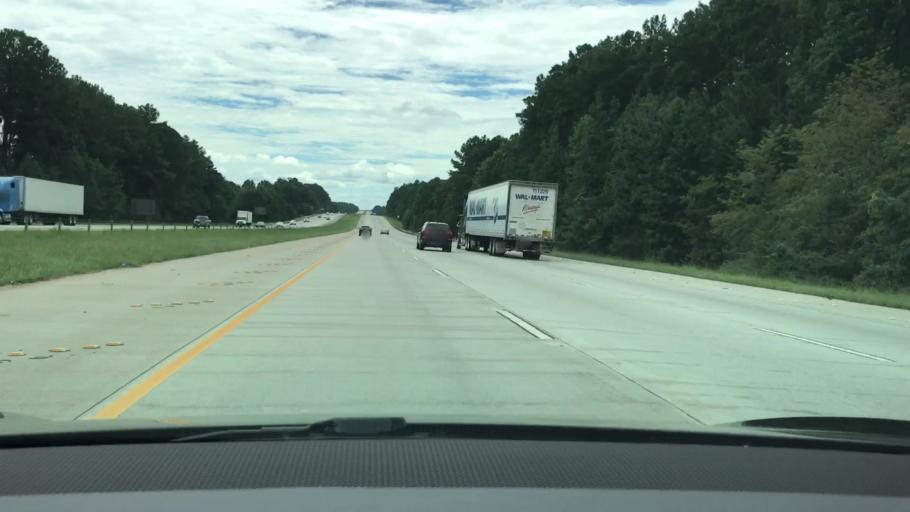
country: US
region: Georgia
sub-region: Coweta County
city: East Newnan
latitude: 33.3088
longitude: -84.7894
